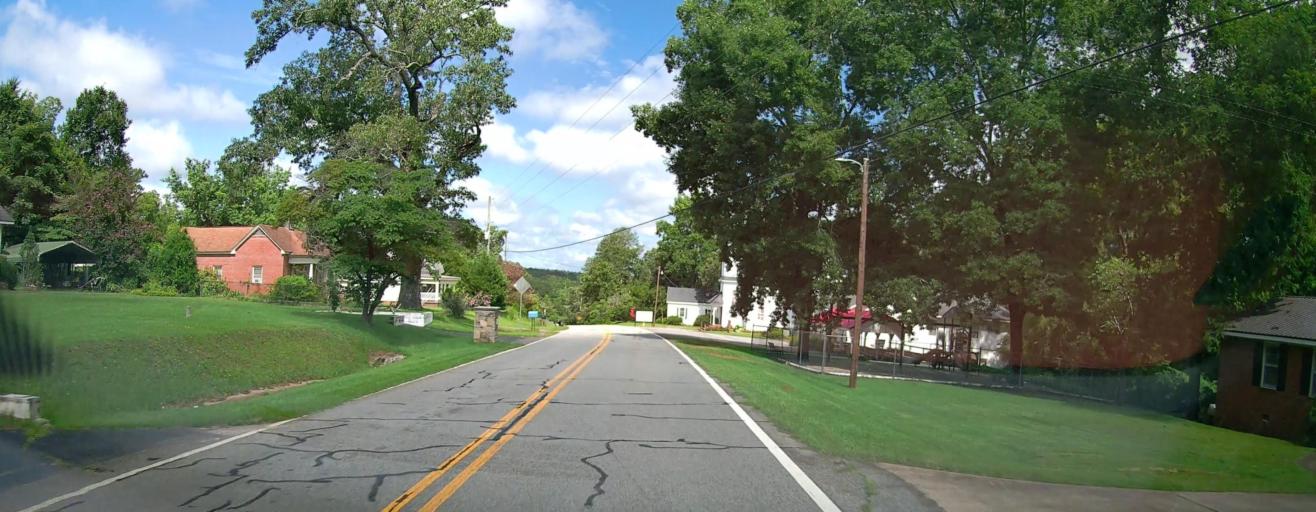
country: US
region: Georgia
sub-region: Peach County
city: Byron
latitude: 32.6026
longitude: -83.7894
